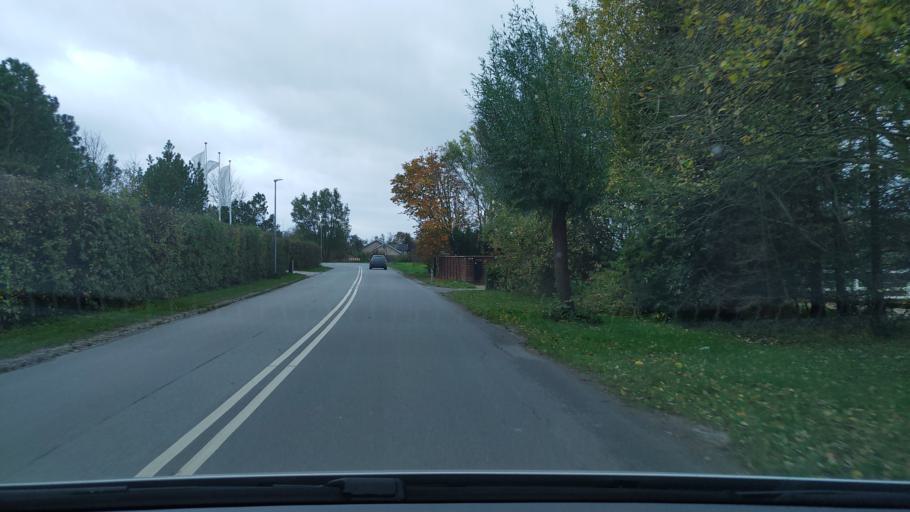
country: DK
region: Capital Region
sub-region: Tarnby Kommune
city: Tarnby
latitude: 55.6042
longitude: 12.6052
